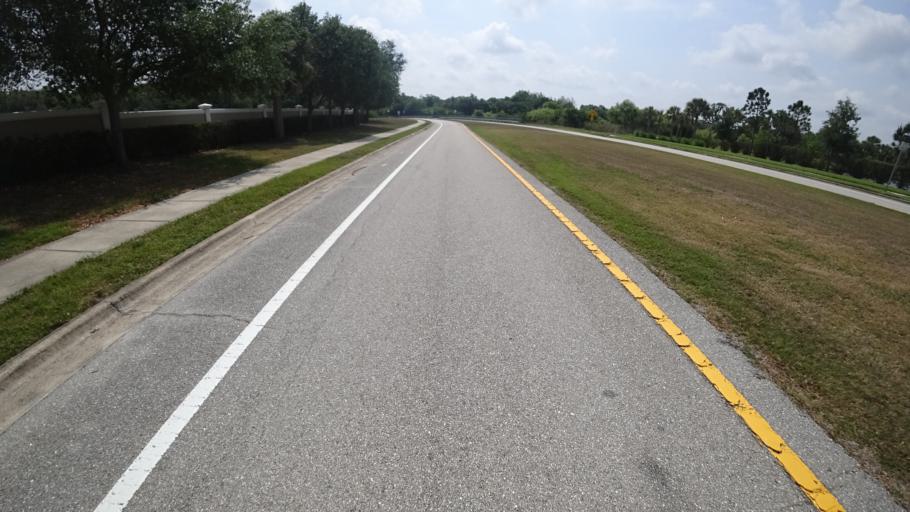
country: US
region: Florida
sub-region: Sarasota County
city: North Sarasota
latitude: 27.4185
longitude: -82.5108
